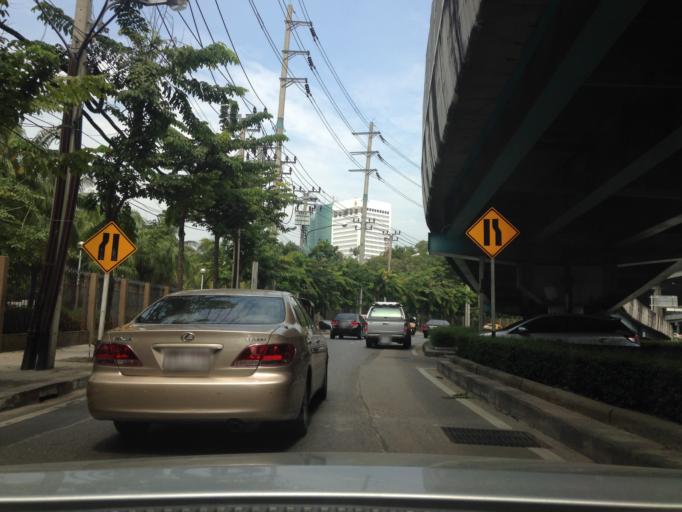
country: TH
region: Bangkok
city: Chatuchak
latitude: 13.8121
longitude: 100.5588
